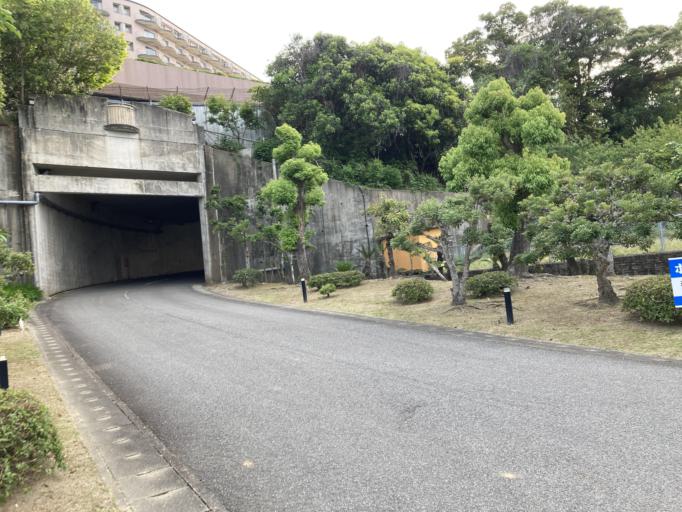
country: JP
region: Wakayama
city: Tanabe
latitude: 33.6835
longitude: 135.3590
